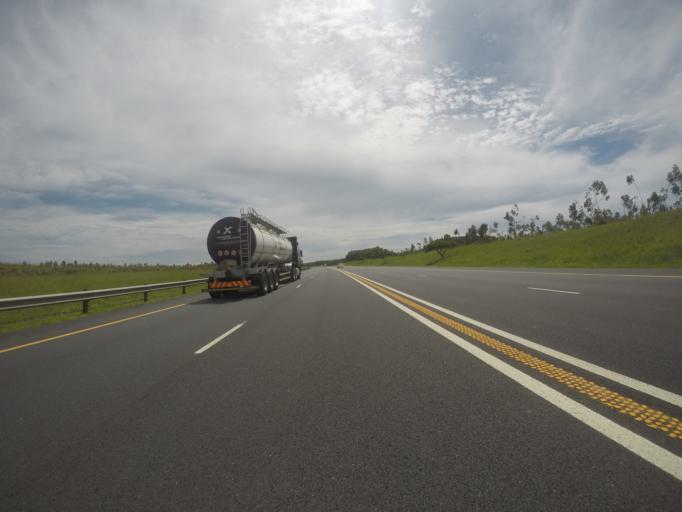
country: ZA
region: KwaZulu-Natal
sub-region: iLembe District Municipality
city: Mandeni
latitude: -29.1620
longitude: 31.5334
